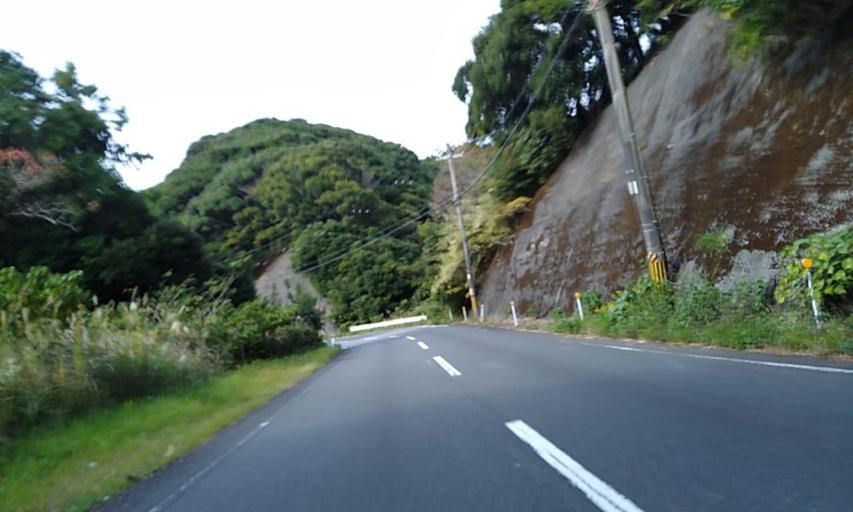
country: JP
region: Wakayama
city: Shingu
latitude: 33.4688
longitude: 135.8250
